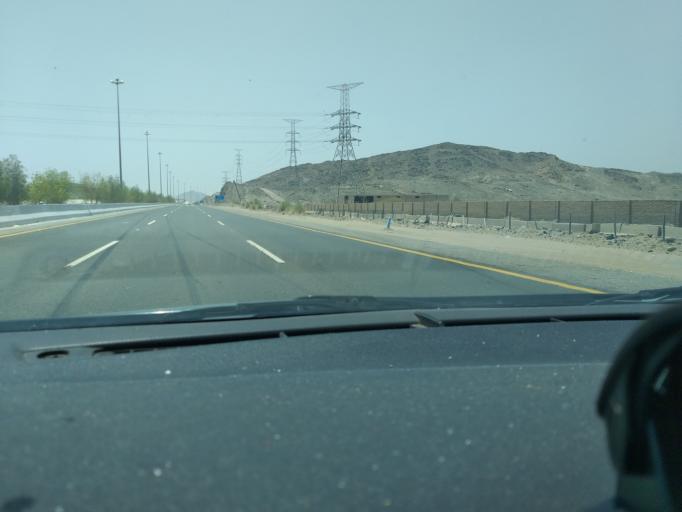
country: SA
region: Makkah
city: Mecca
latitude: 21.3275
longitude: 39.9827
